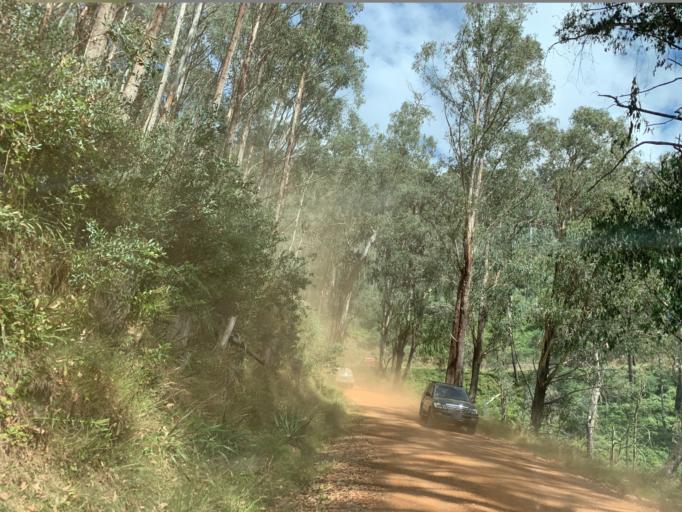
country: AU
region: Victoria
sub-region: Mansfield
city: Mansfield
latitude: -37.0970
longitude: 146.5390
